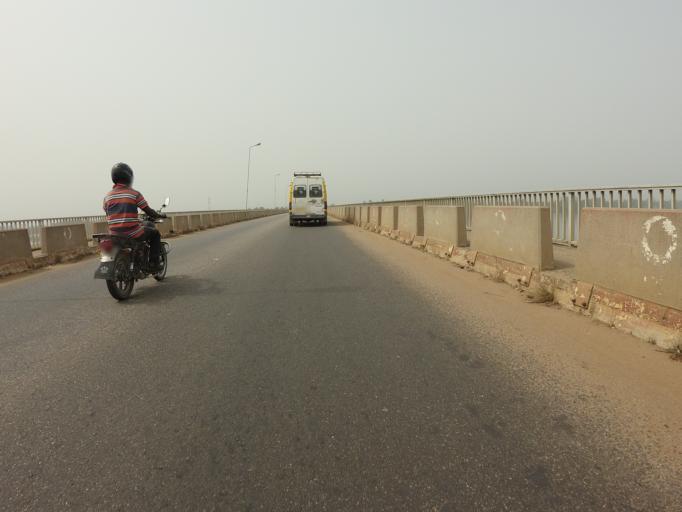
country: GH
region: Volta
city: Anloga
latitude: 5.9958
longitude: 0.5864
